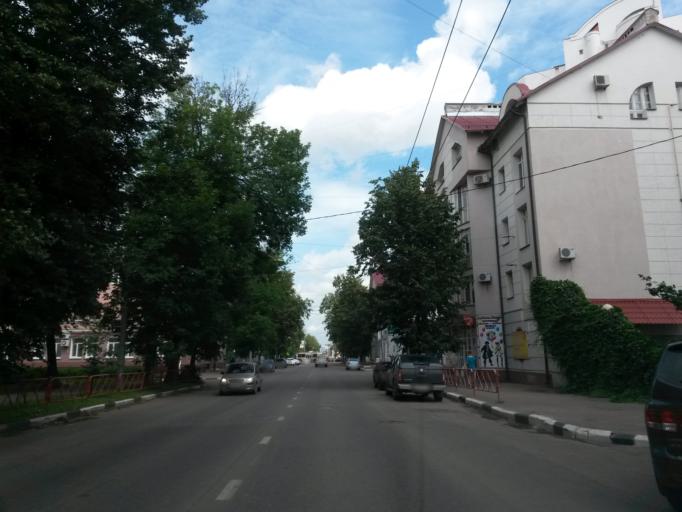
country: RU
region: Jaroslavl
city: Yaroslavl
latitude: 57.6341
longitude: 39.8808
